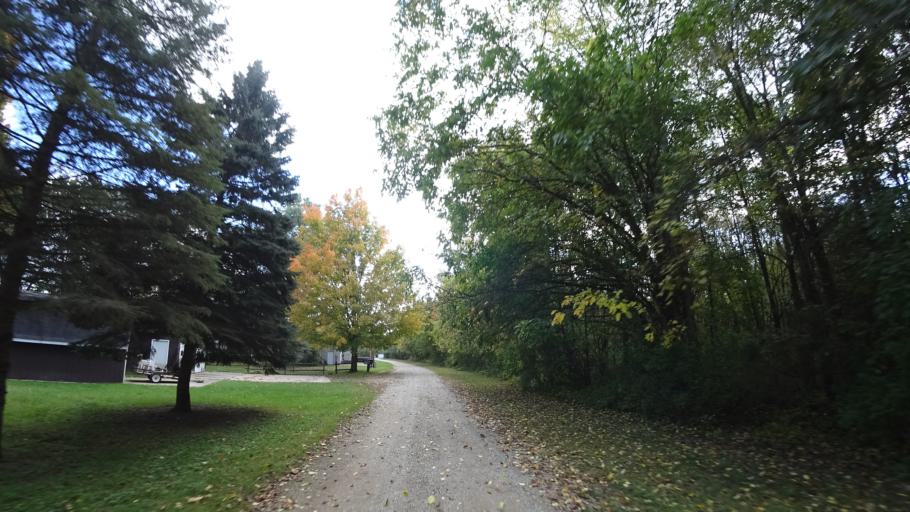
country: US
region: Michigan
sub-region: Saint Joseph County
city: Three Rivers
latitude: 41.9506
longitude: -85.5873
